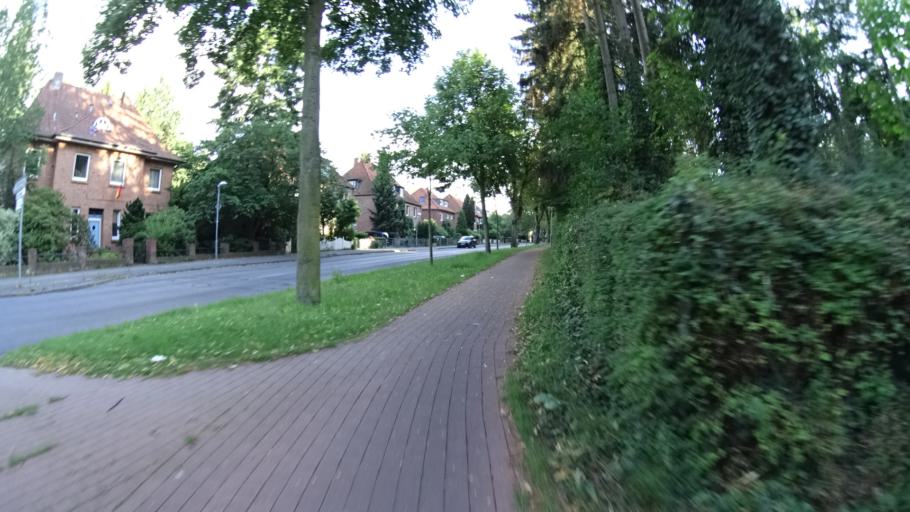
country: DE
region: Lower Saxony
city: Lueneburg
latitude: 53.2367
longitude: 10.3985
